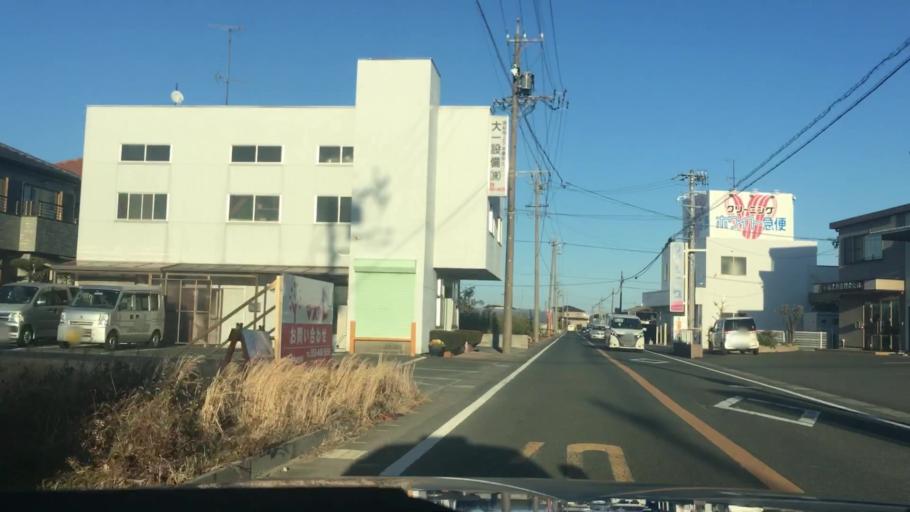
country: JP
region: Shizuoka
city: Hamamatsu
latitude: 34.7399
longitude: 137.6717
